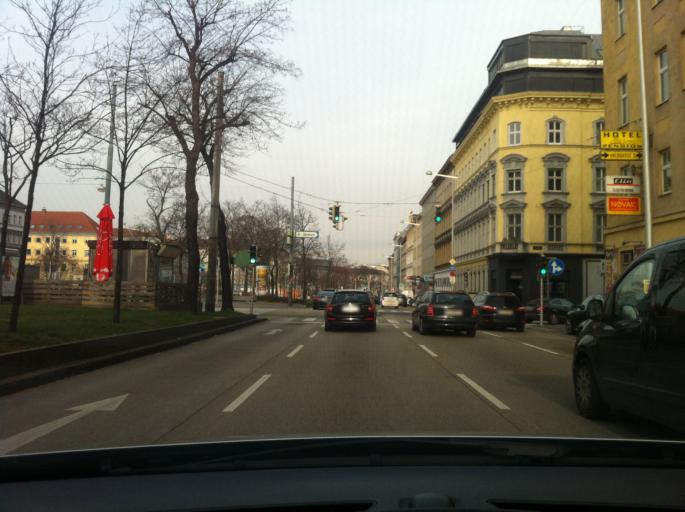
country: AT
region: Vienna
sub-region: Wien Stadt
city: Vienna
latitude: 48.2038
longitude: 16.3376
